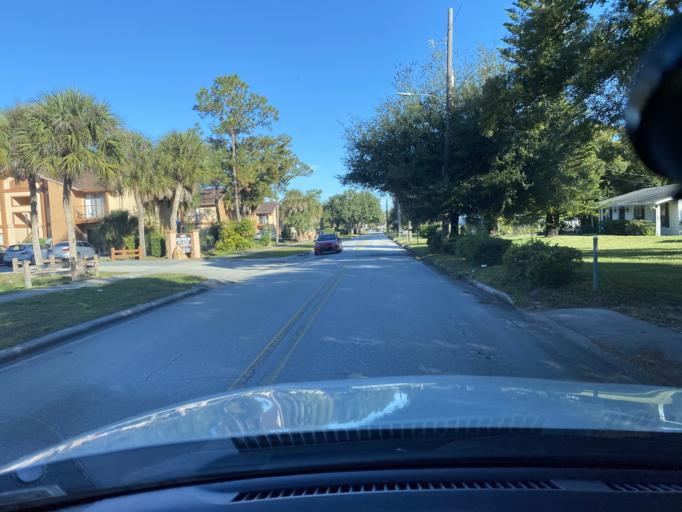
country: US
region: Florida
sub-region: Orange County
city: Azalea Park
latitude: 28.5190
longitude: -81.3062
